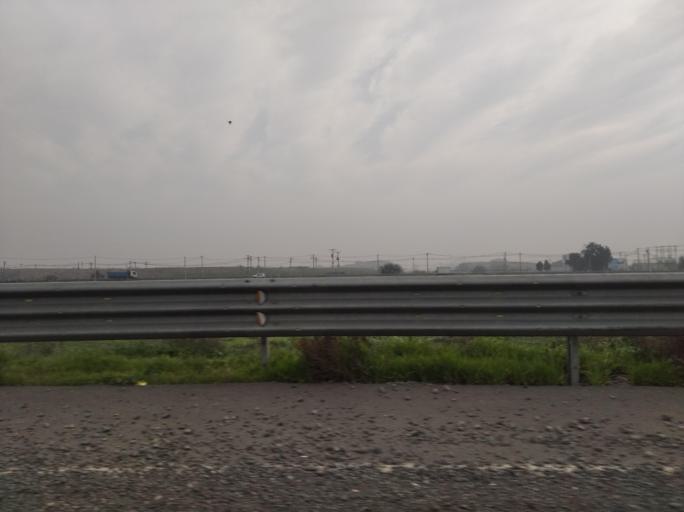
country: CL
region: Santiago Metropolitan
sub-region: Provincia de Santiago
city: Lo Prado
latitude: -33.3659
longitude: -70.8006
